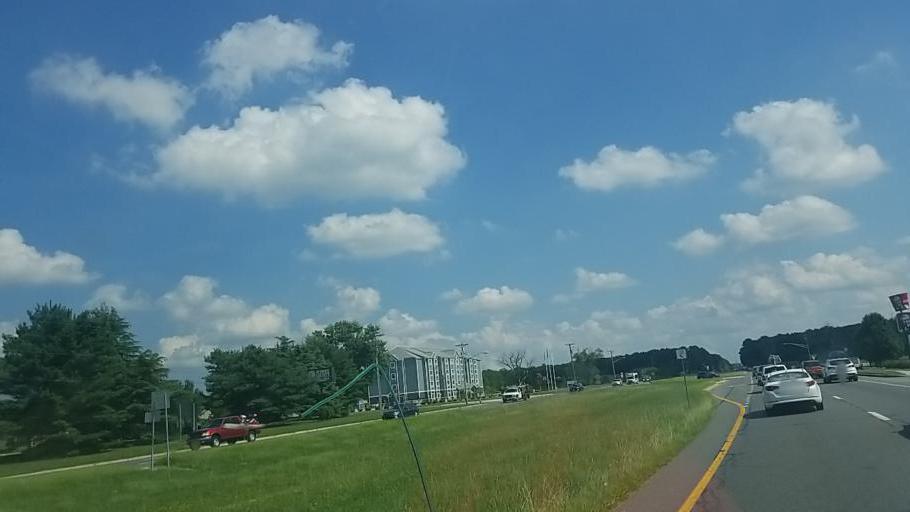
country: US
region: Delaware
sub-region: Sussex County
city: Georgetown
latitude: 38.6811
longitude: -75.3955
